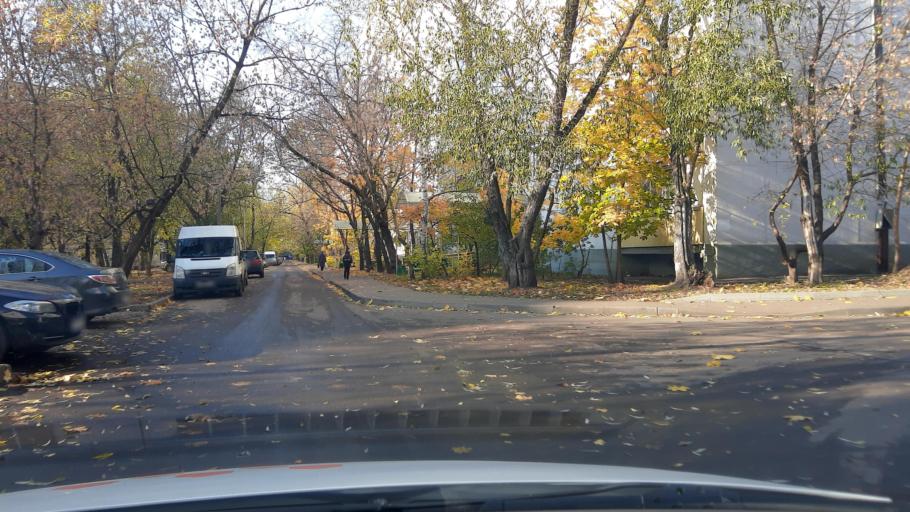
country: RU
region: Moscow
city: Vykhino-Zhulebino
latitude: 55.7127
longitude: 37.8110
